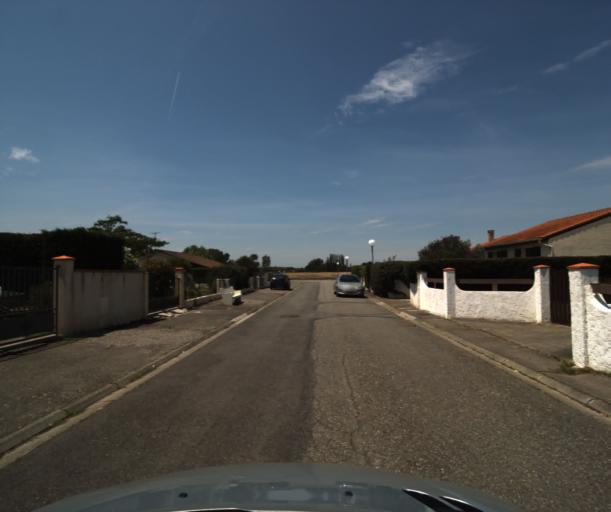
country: FR
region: Midi-Pyrenees
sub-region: Departement de la Haute-Garonne
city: Labastidette
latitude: 43.4645
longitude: 1.2460
